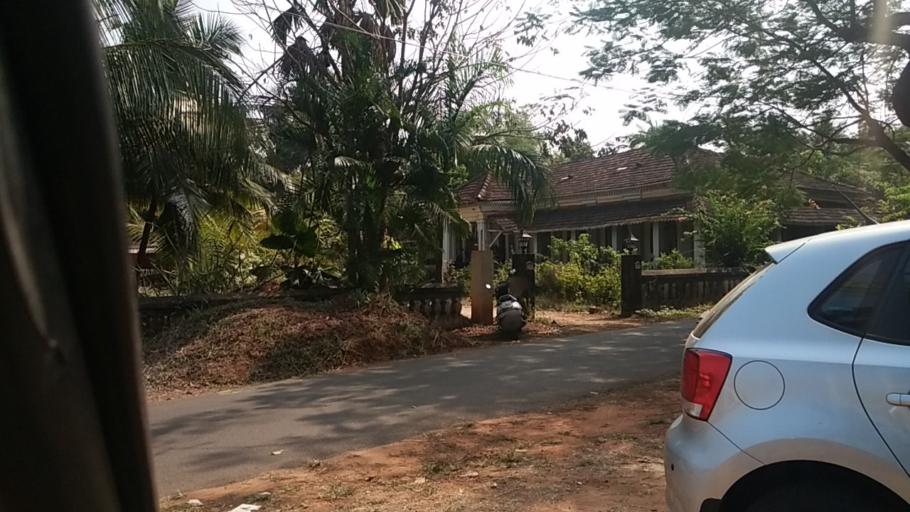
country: IN
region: Goa
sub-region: South Goa
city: Chinchinim
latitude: 15.2032
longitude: 73.9555
